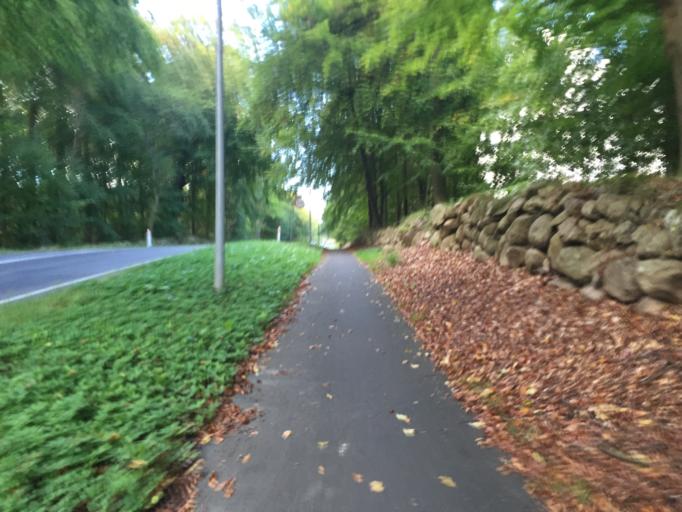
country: DK
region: Capital Region
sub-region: Fureso Kommune
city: Vaerlose
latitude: 55.7707
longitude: 12.3903
